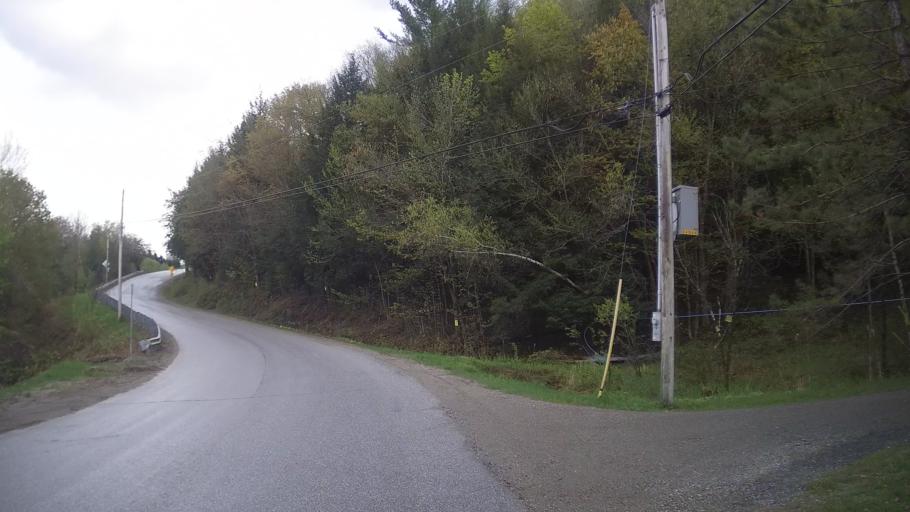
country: US
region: Vermont
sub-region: Franklin County
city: Richford
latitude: 44.9837
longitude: -72.6652
